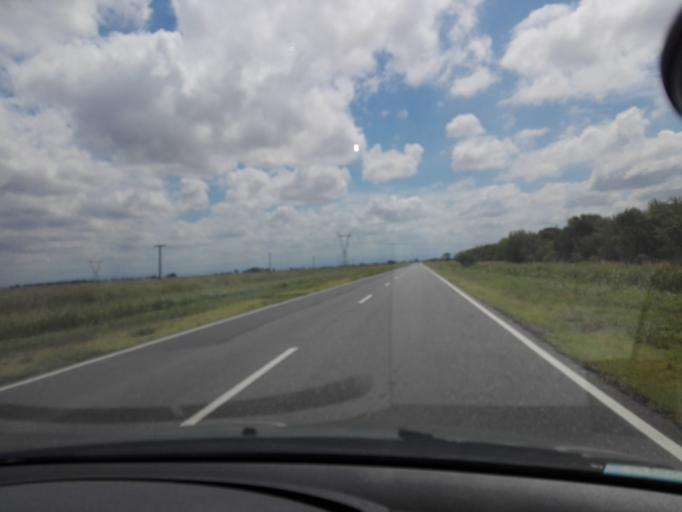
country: AR
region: Cordoba
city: Toledo
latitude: -31.6459
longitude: -64.0341
